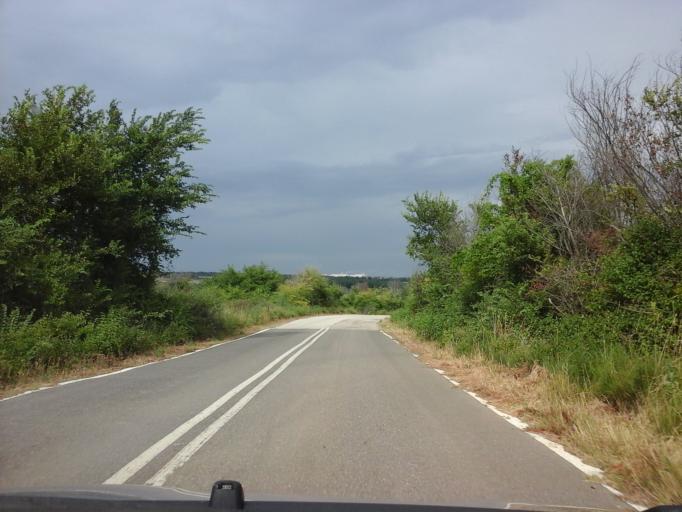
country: GR
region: East Macedonia and Thrace
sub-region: Nomos Evrou
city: Tychero
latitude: 41.0229
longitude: 26.2275
